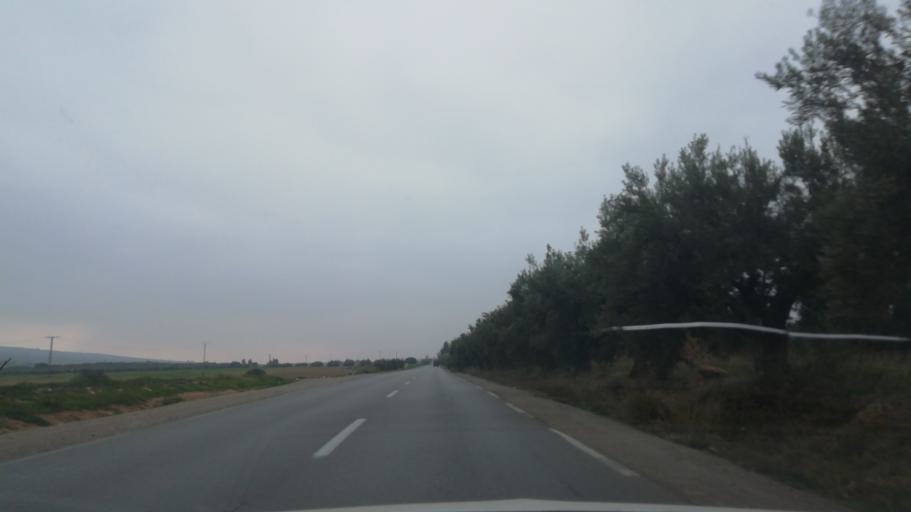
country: DZ
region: Sidi Bel Abbes
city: Sfizef
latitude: 35.2647
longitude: -0.1680
